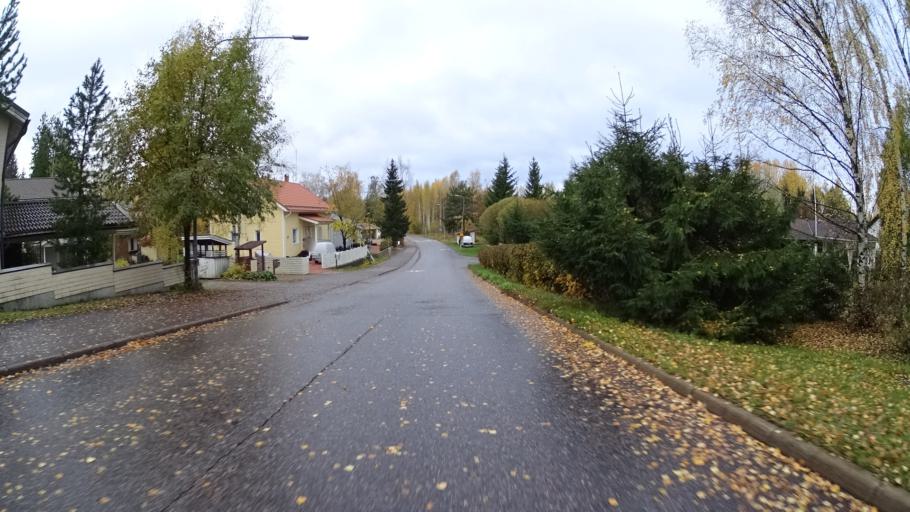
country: FI
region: Uusimaa
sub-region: Helsinki
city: Kilo
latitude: 60.2640
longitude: 24.8205
